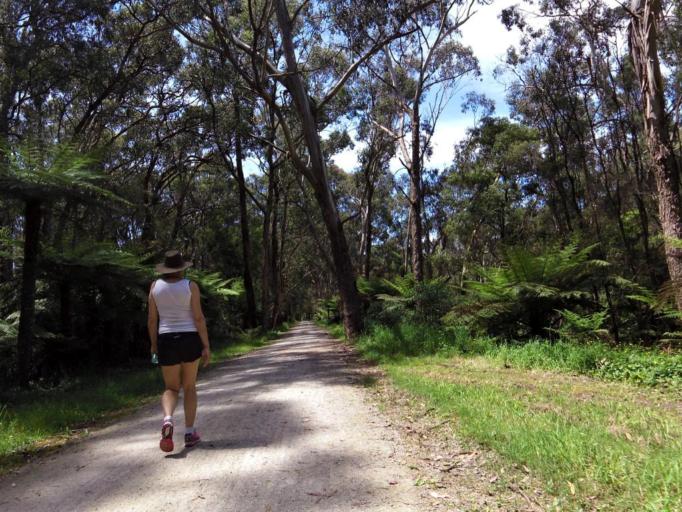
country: AU
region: Victoria
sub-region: Yarra Ranges
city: Mount Evelyn
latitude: -37.7818
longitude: 145.4023
